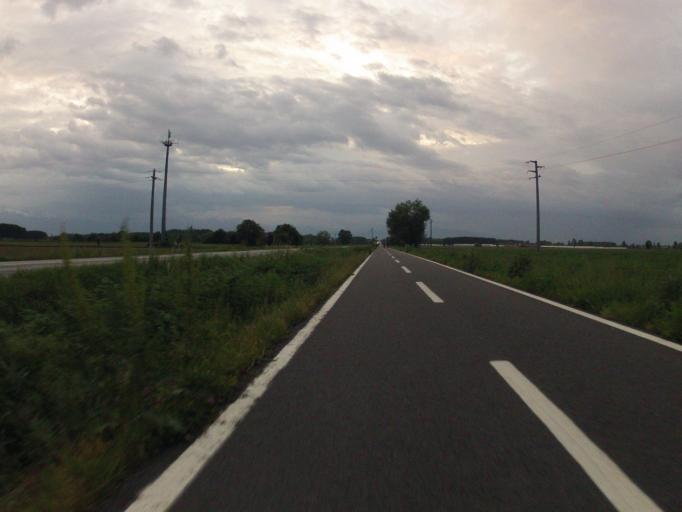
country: IT
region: Piedmont
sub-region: Provincia di Cuneo
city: Moretta
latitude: 44.7733
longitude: 7.5221
